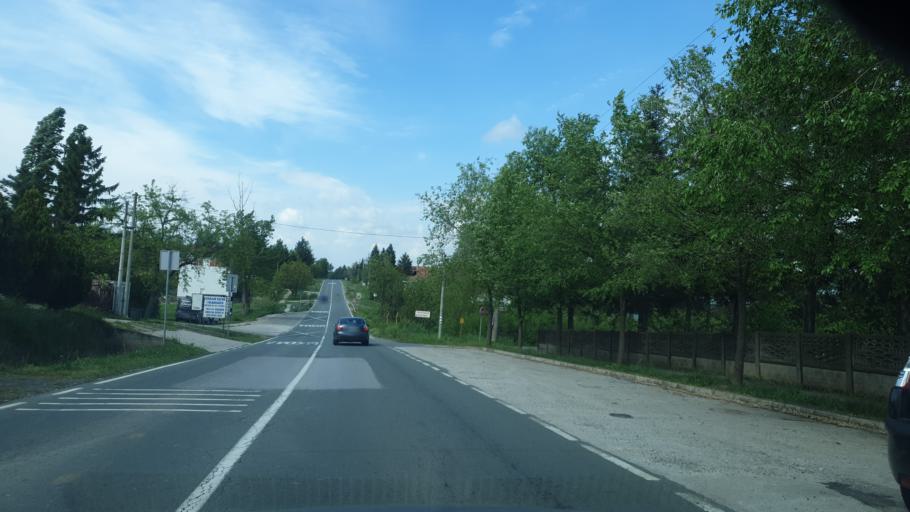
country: RS
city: Stubline
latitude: 44.5748
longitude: 20.1523
